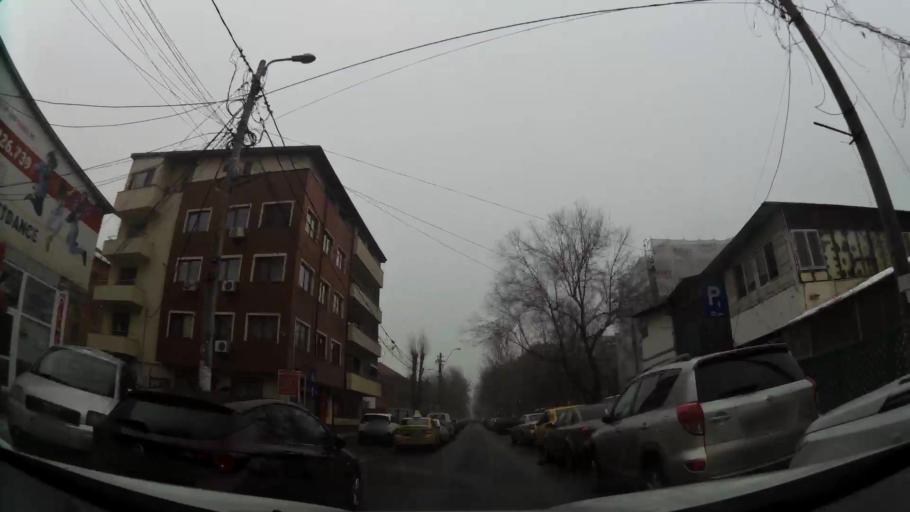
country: RO
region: Ilfov
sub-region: Comuna Chiajna
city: Rosu
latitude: 44.4361
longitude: 26.0285
